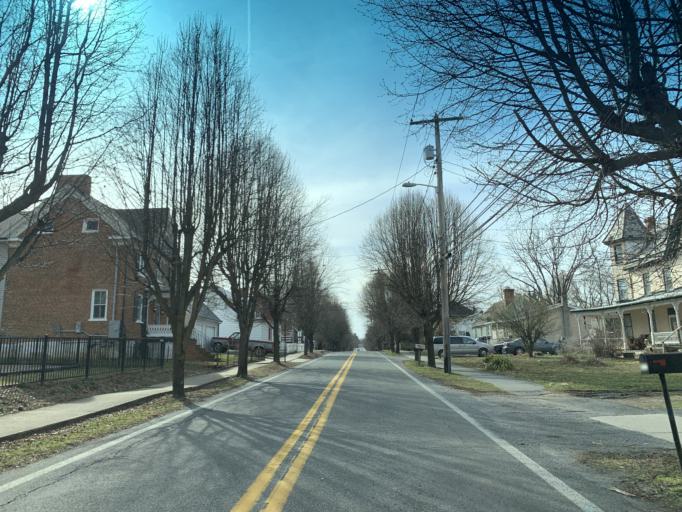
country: US
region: West Virginia
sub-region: Jefferson County
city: Bolivar
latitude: 39.3246
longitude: -77.7512
